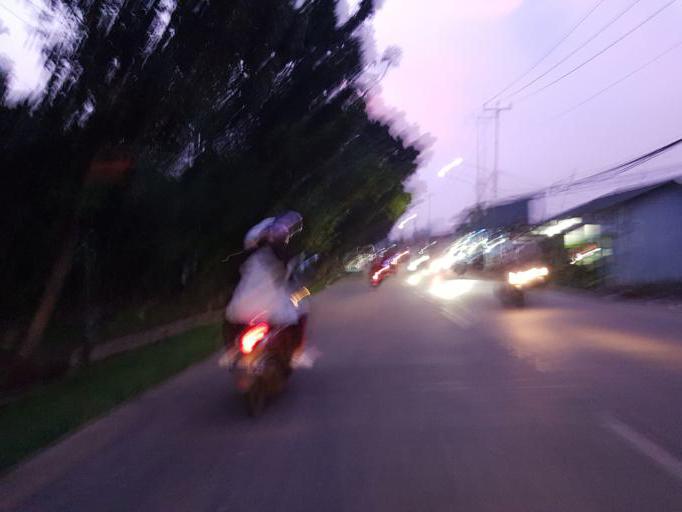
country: ID
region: West Java
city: Serpong
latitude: -6.3262
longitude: 106.6709
